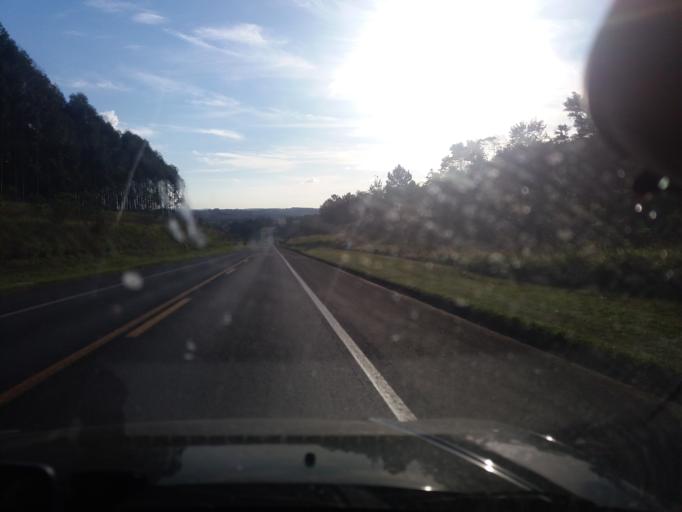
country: BR
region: Sao Paulo
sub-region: Buri
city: Buri
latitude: -23.9367
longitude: -48.6234
